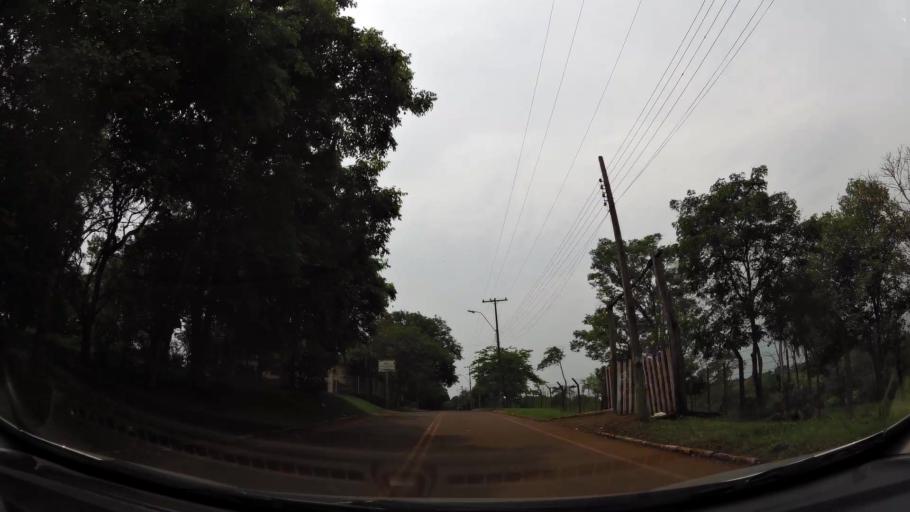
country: PY
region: Alto Parana
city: Presidente Franco
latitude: -25.5590
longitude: -54.6304
